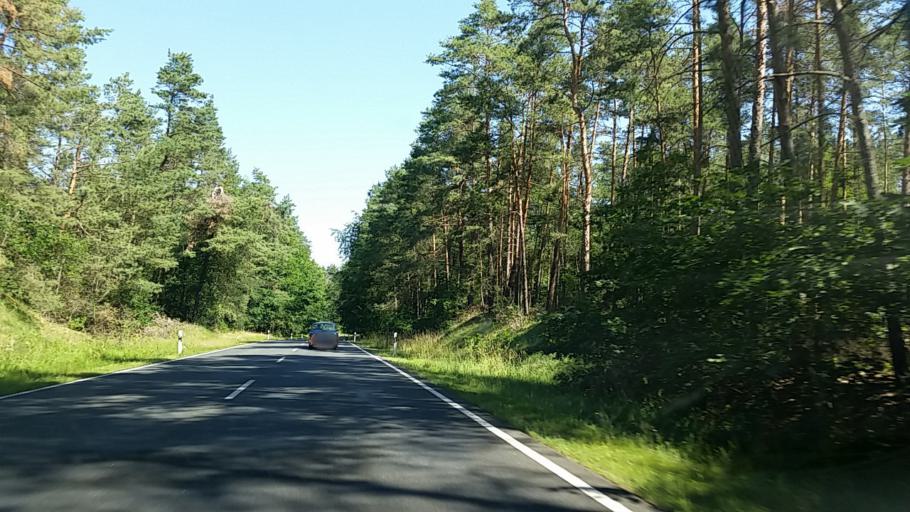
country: DE
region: Saxony-Anhalt
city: Kemberg
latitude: 51.6870
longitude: 12.6127
